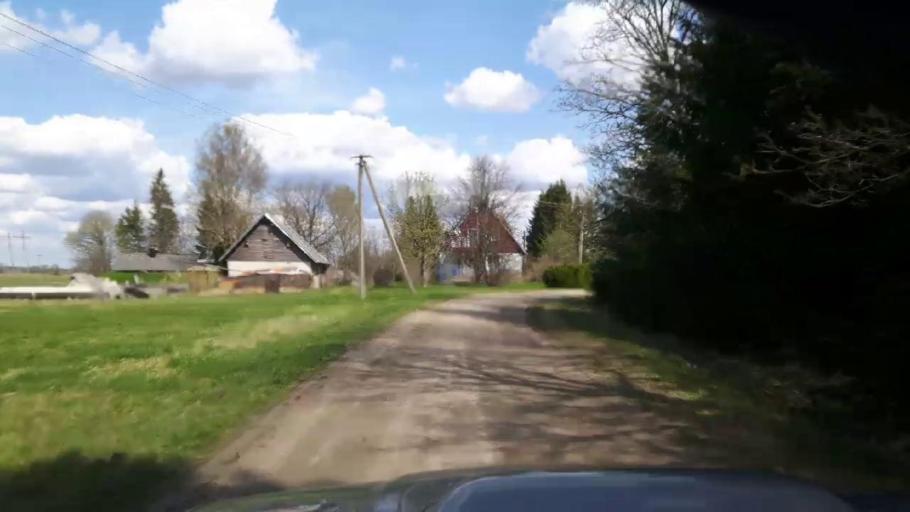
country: EE
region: Paernumaa
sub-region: Tootsi vald
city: Tootsi
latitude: 58.5649
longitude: 24.8900
